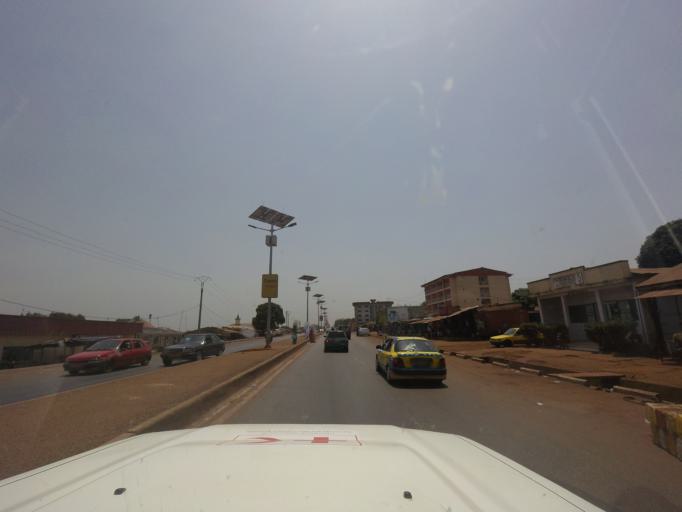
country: GN
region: Conakry
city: Conakry
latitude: 9.6324
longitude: -13.5731
